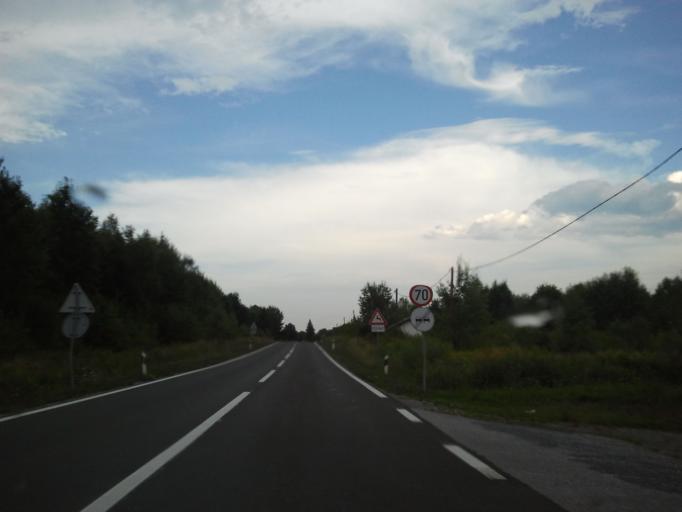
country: HR
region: Sisacko-Moslavacka
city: Gvozd
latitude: 45.3350
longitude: 15.9784
